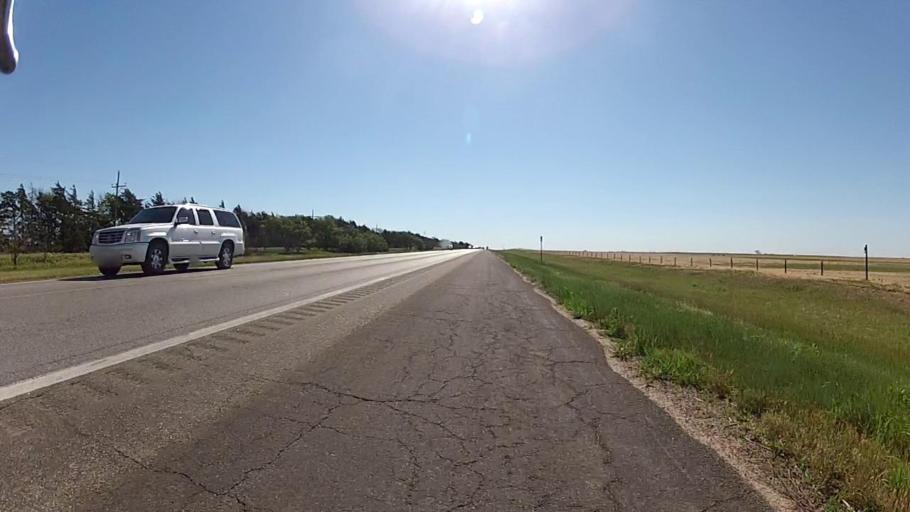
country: US
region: Kansas
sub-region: Kiowa County
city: Greensburg
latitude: 37.5865
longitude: -99.5814
